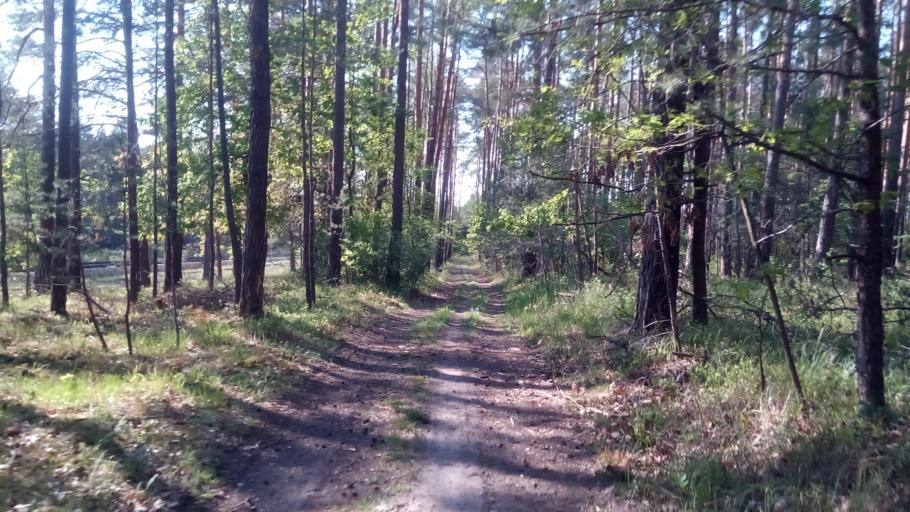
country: PL
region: Opole Voivodeship
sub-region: Powiat opolski
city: Tarnow Opolski
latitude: 50.5863
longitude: 18.0513
